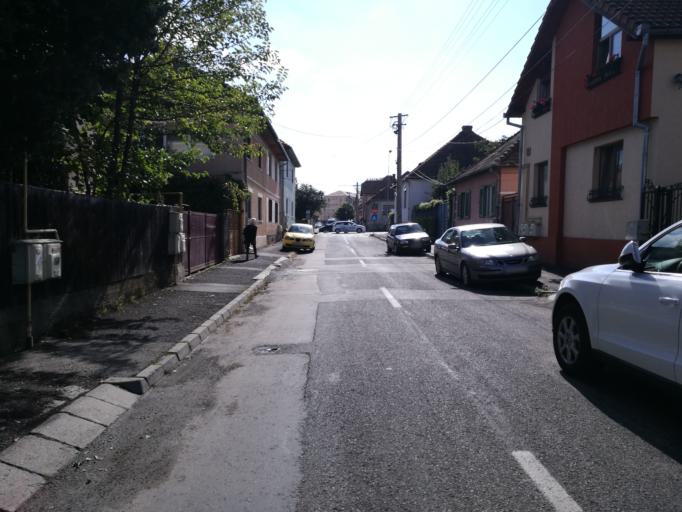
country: RO
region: Sibiu
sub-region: Municipiul Sibiu
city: Sibiu
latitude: 45.7834
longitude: 24.1591
